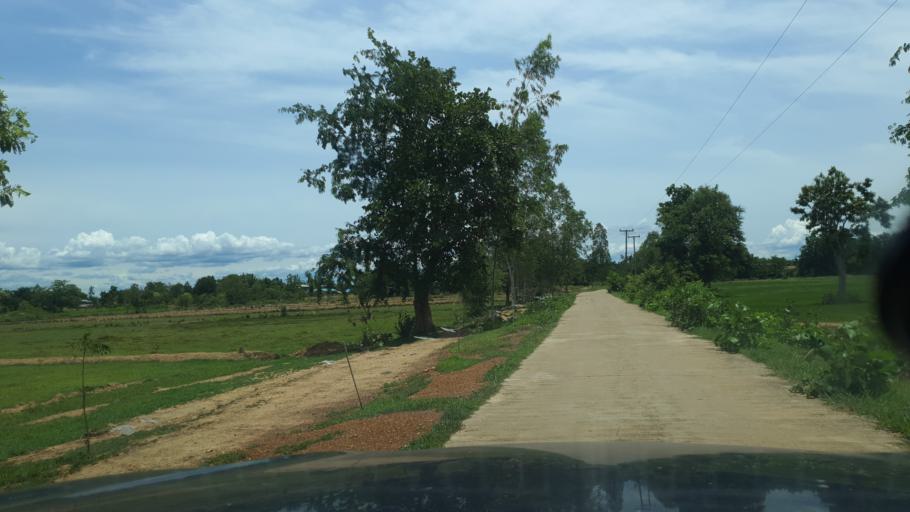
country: TH
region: Sukhothai
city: Ban Na
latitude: 17.0897
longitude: 99.6870
